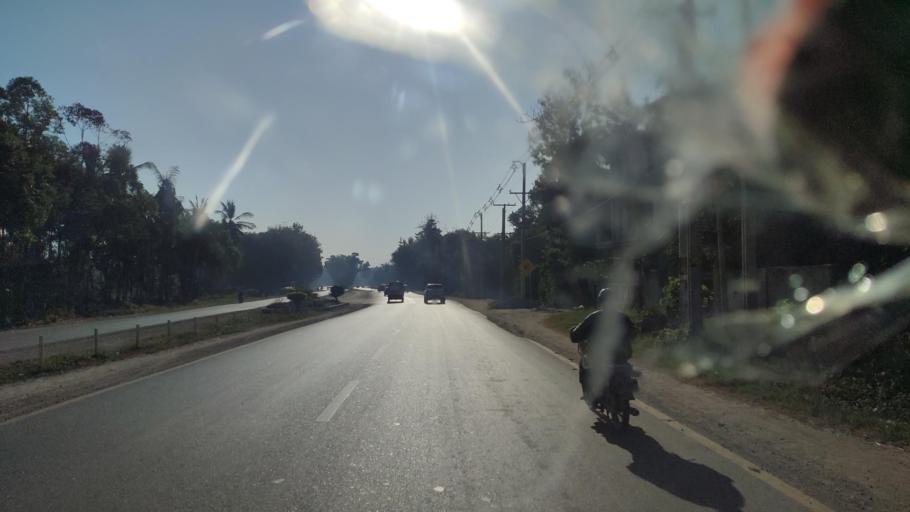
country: MM
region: Mandalay
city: Mandalay
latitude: 21.9156
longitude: 96.1671
